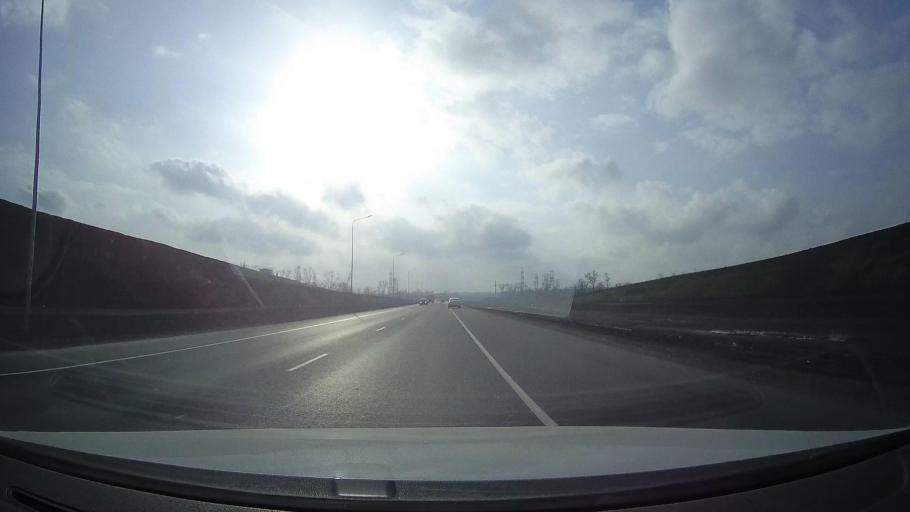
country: RU
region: Rostov
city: Grushevskaya
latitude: 47.4146
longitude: 39.8602
